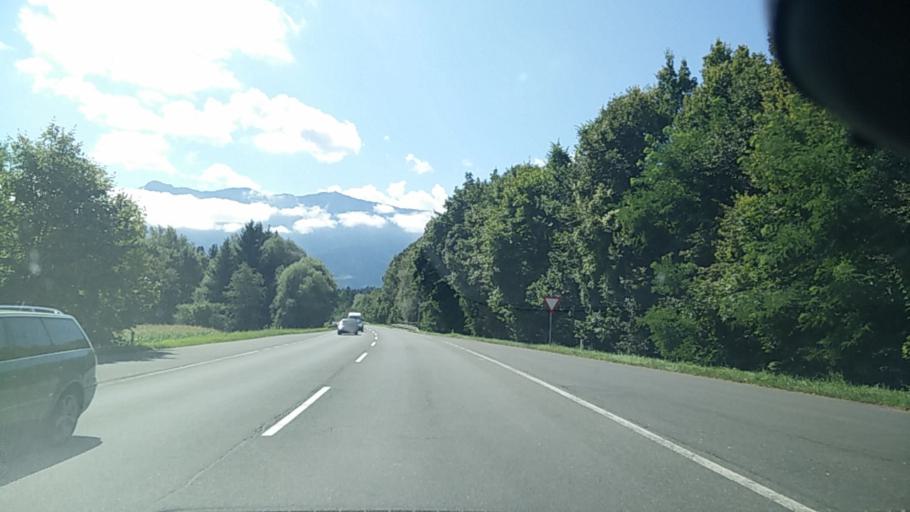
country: AT
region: Carinthia
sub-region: Villach Stadt
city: Villach
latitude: 46.5869
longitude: 13.8334
